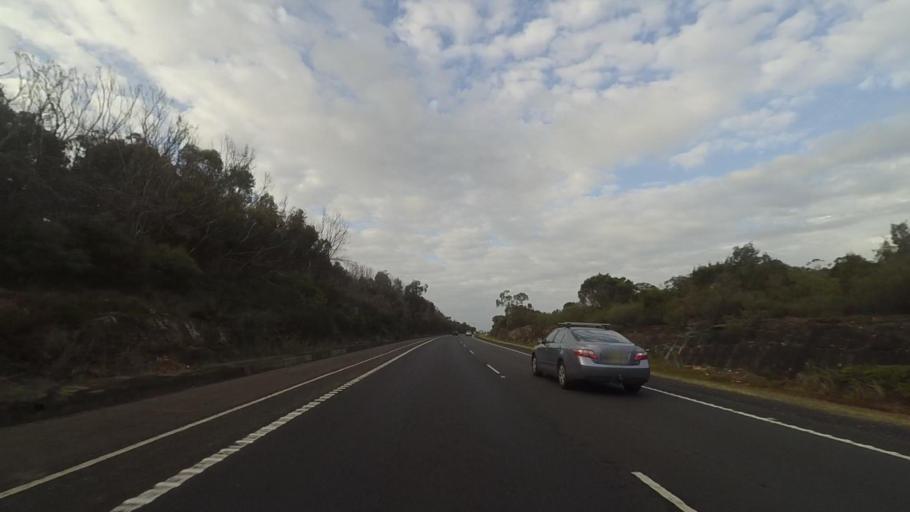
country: AU
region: New South Wales
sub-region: Wollongong
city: Bulli
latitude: -34.2670
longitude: 150.9269
